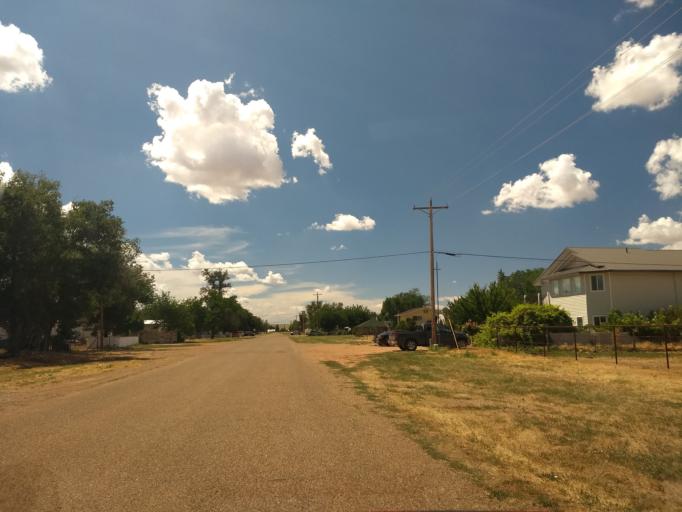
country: US
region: Arizona
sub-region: Coconino County
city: Fredonia
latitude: 36.9503
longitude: -112.5243
